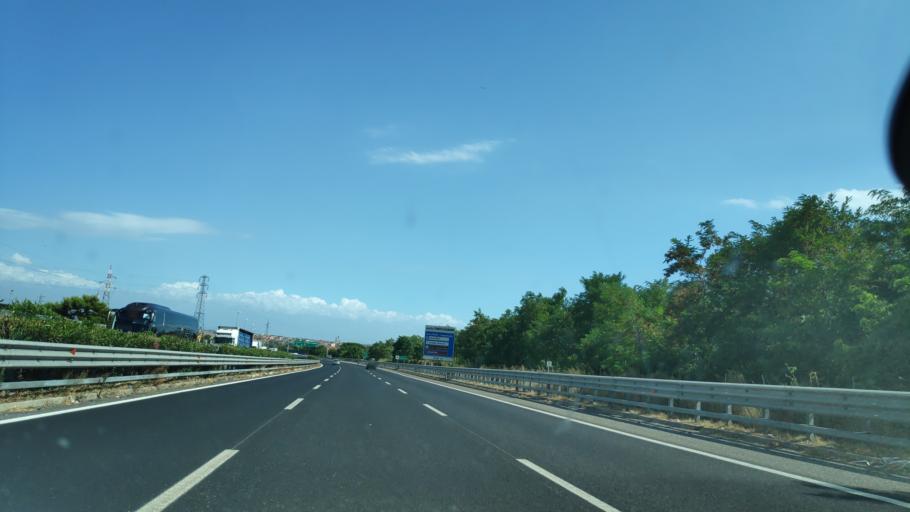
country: IT
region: Campania
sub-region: Provincia di Salerno
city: Pontecagnano
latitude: 40.6597
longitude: 14.8610
